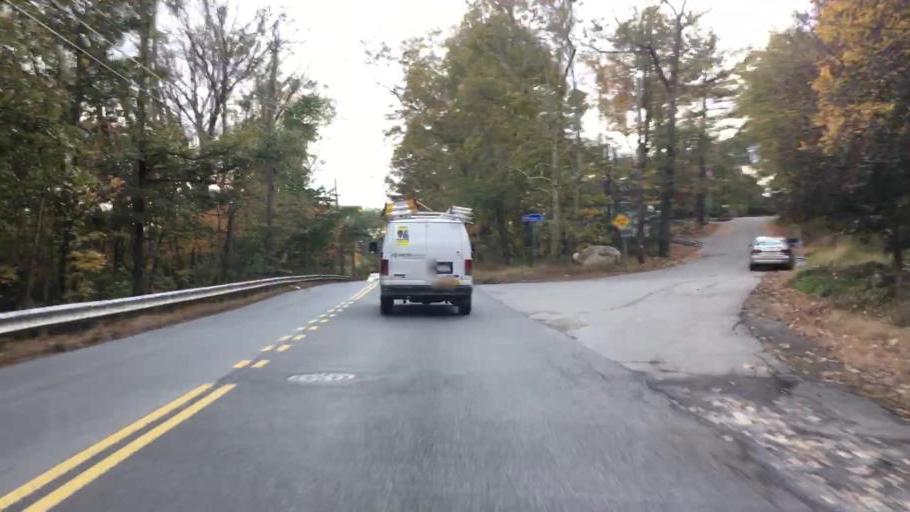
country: US
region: Massachusetts
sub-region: Middlesex County
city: Ashland
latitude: 42.2763
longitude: -71.4604
